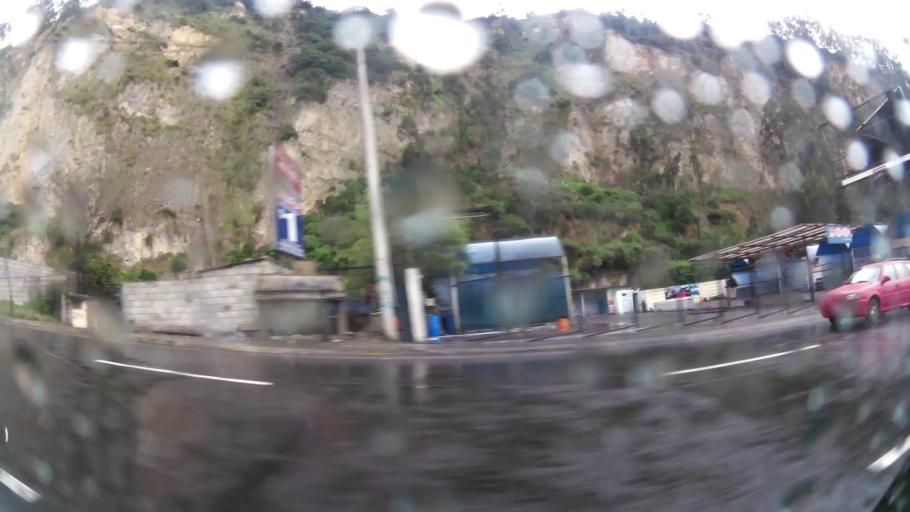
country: EC
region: Pichincha
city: Quito
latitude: -0.1501
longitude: -78.4554
